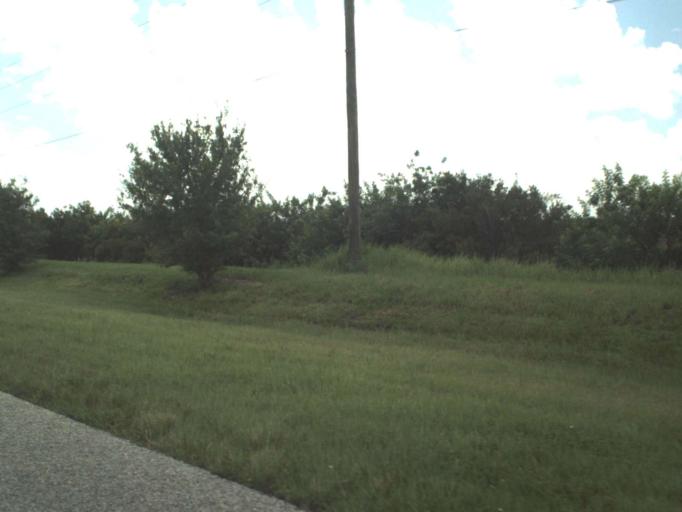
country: US
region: Florida
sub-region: Indian River County
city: Fellsmere
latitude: 27.6418
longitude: -80.7562
